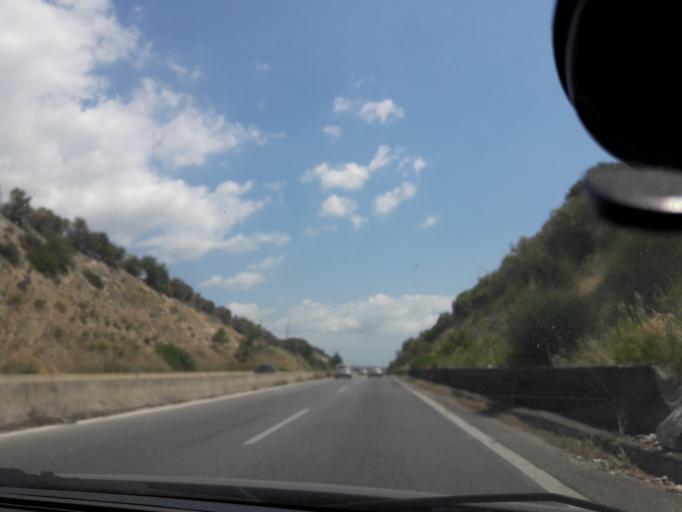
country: GR
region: Central Macedonia
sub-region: Nomos Chalkidikis
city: Nea Kallikrateia
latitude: 40.3127
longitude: 23.1031
